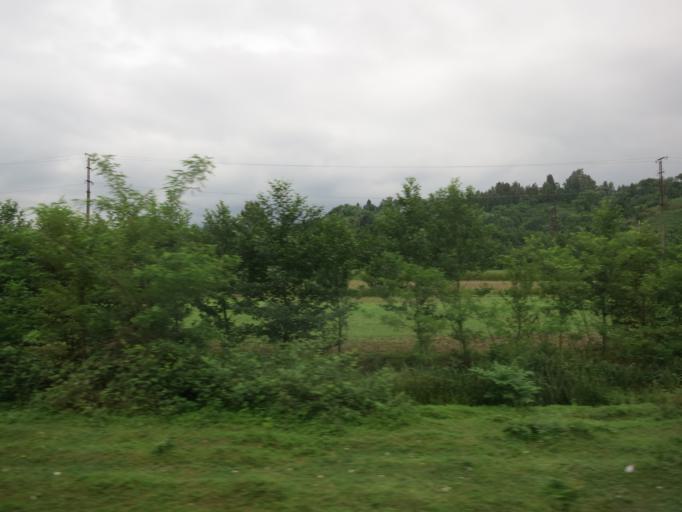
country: GE
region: Ajaria
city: Kobuleti
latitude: 41.7845
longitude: 41.7657
